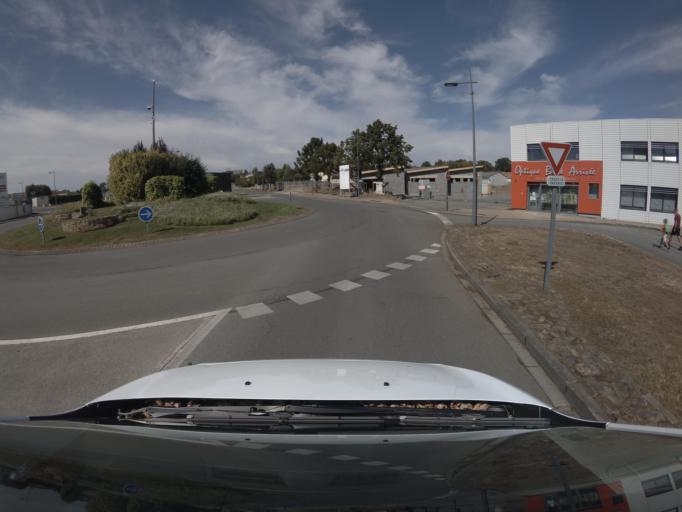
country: FR
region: Poitou-Charentes
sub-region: Departement des Deux-Sevres
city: Nueil-les-Aubiers
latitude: 46.9460
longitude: -0.5942
